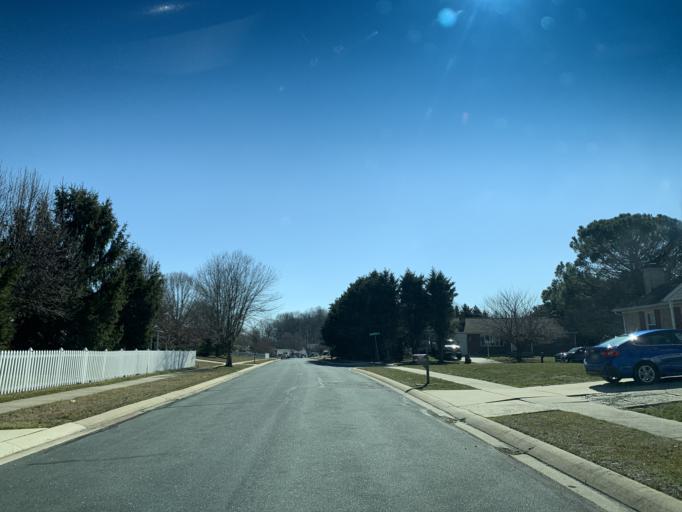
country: US
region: Maryland
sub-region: Harford County
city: South Bel Air
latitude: 39.5412
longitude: -76.2960
